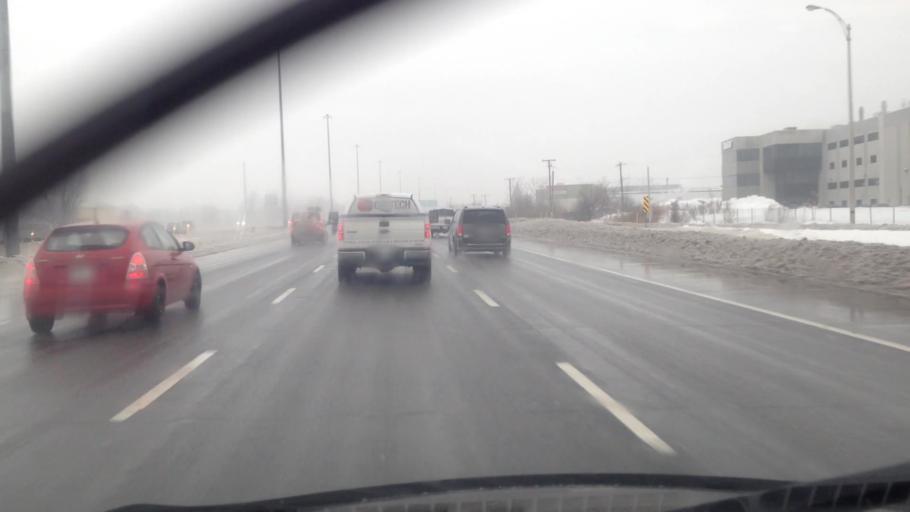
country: CA
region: Quebec
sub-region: Laurentides
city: Boisbriand
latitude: 45.6192
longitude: -73.8269
